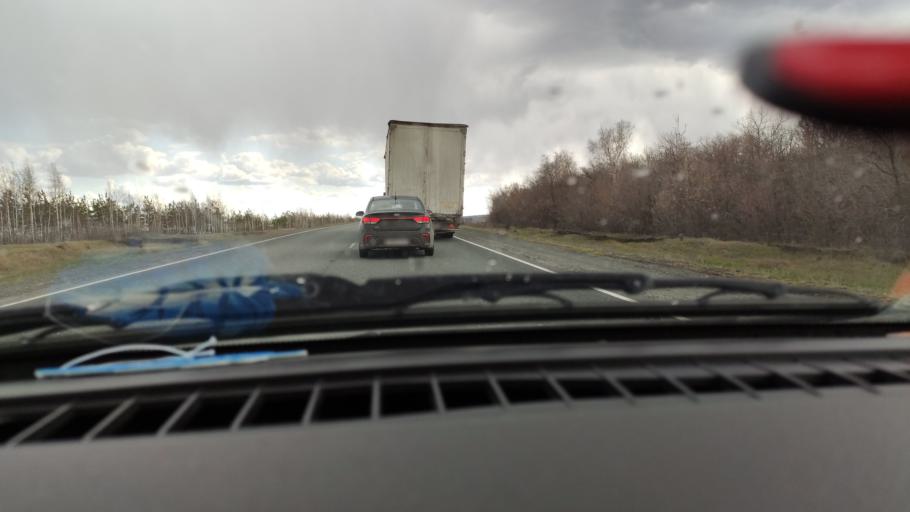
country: RU
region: Saratov
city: Balakovo
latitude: 52.1611
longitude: 47.8221
